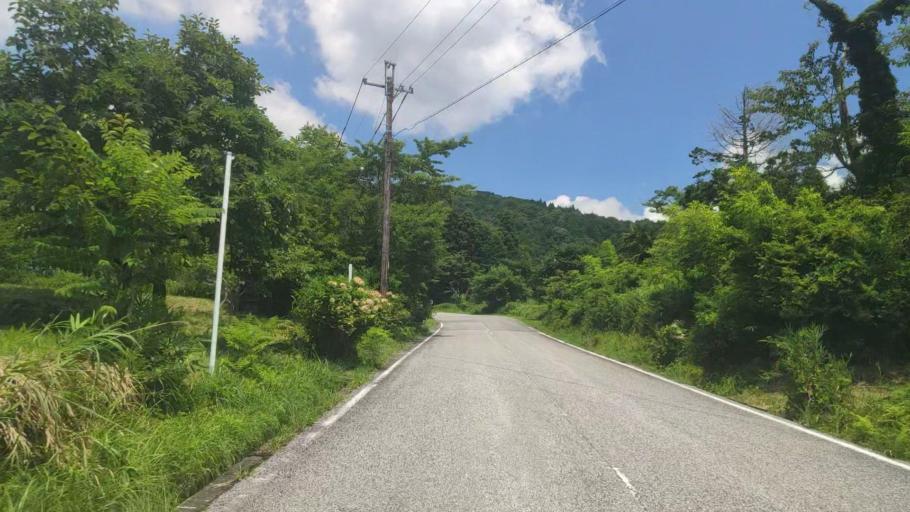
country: JP
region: Gifu
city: Tarui
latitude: 35.3730
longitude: 136.4491
